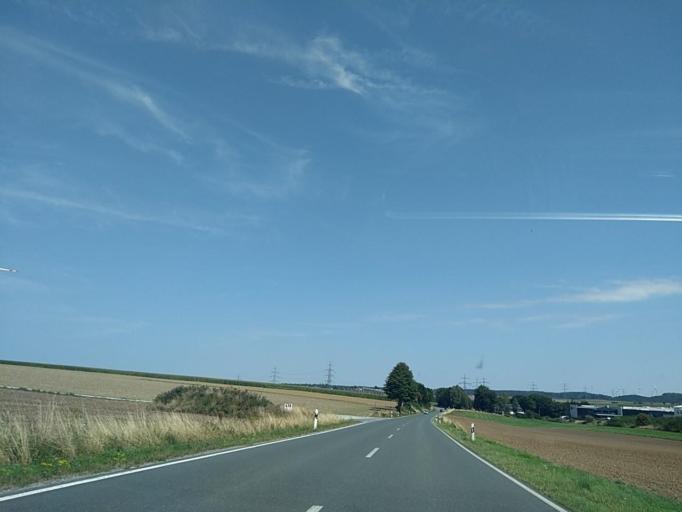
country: DE
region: North Rhine-Westphalia
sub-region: Regierungsbezirk Arnsberg
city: Brilon
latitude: 51.4209
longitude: 8.6150
